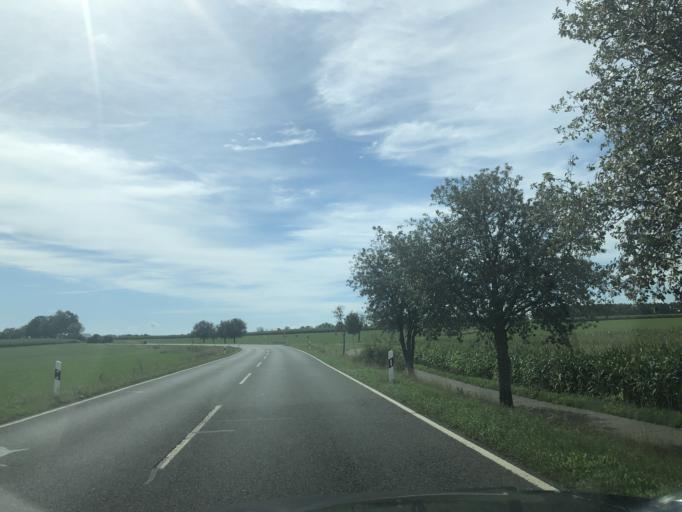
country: DE
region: Bavaria
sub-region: Upper Palatinate
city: Speinshart
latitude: 49.7717
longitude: 11.8138
